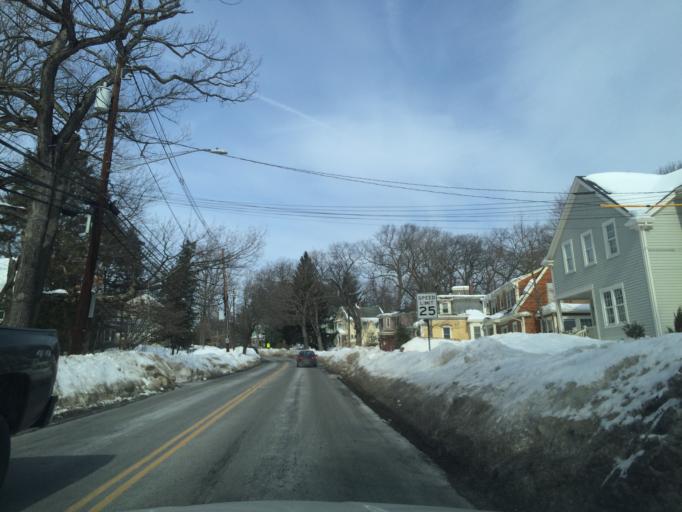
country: US
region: Massachusetts
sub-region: Middlesex County
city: Waltham
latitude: 42.3392
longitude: -71.2512
